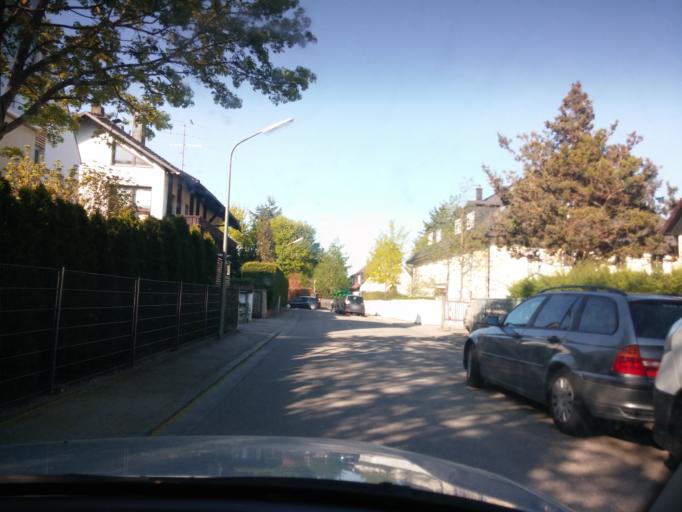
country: DE
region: Bavaria
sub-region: Upper Bavaria
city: Neubiberg
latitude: 48.1177
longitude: 11.6779
